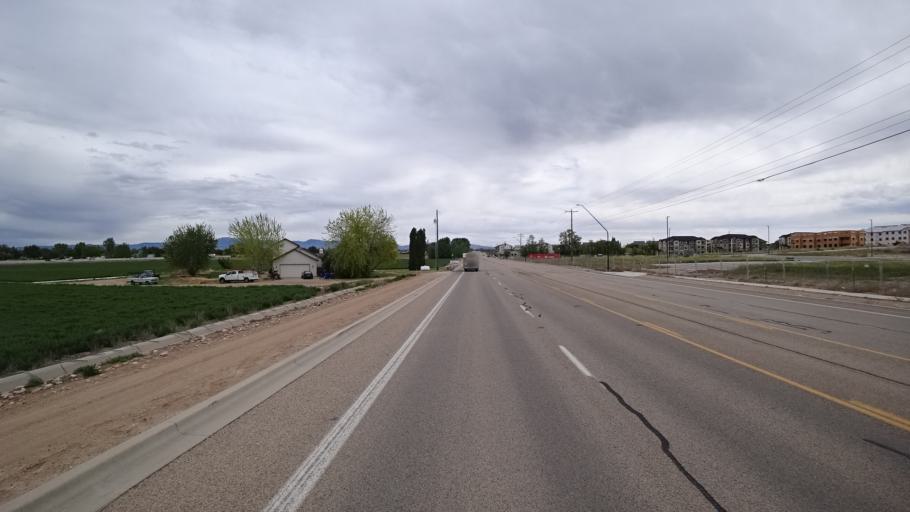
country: US
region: Idaho
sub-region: Ada County
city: Meridian
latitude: 43.5903
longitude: -116.4242
